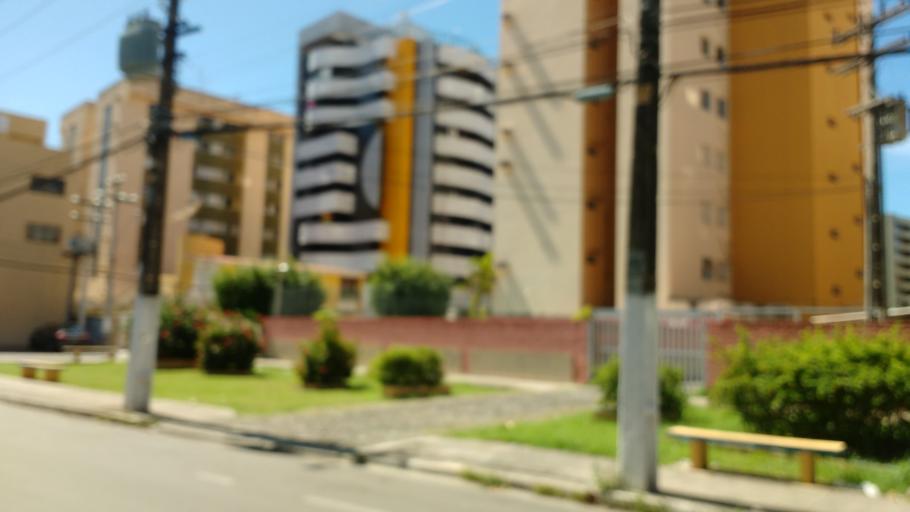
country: BR
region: Alagoas
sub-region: Maceio
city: Maceio
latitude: -9.6599
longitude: -35.7074
